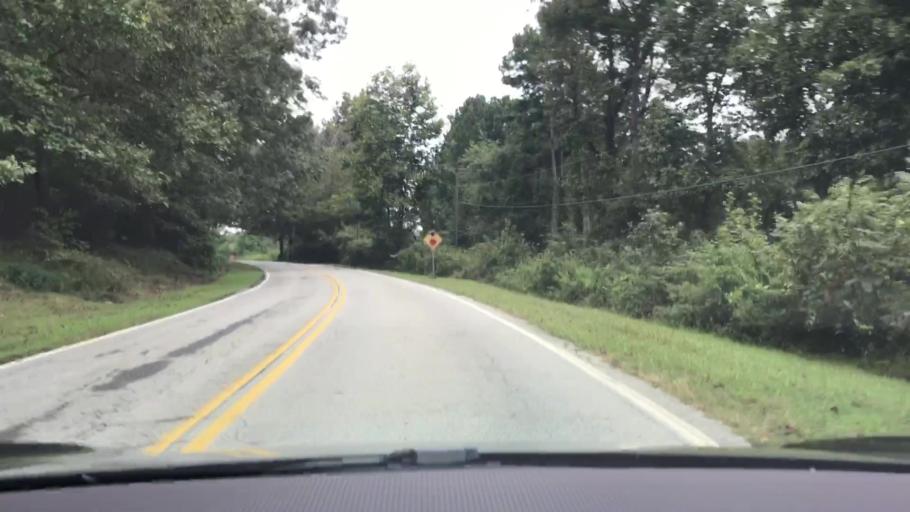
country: US
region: Georgia
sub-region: Barrow County
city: Auburn
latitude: 34.0713
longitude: -83.8419
